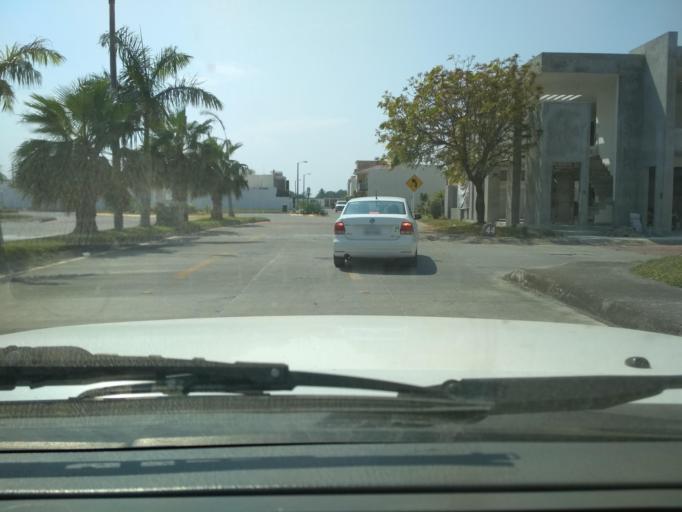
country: MX
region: Veracruz
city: Boca del Rio
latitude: 19.1045
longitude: -96.1244
